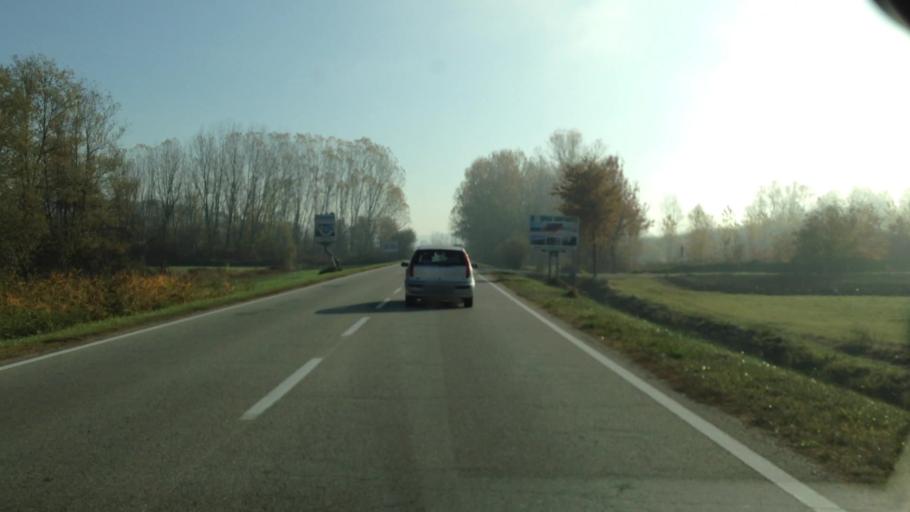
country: IT
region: Piedmont
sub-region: Provincia di Asti
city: Vigliano d'Asti
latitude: 44.8243
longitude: 8.2190
